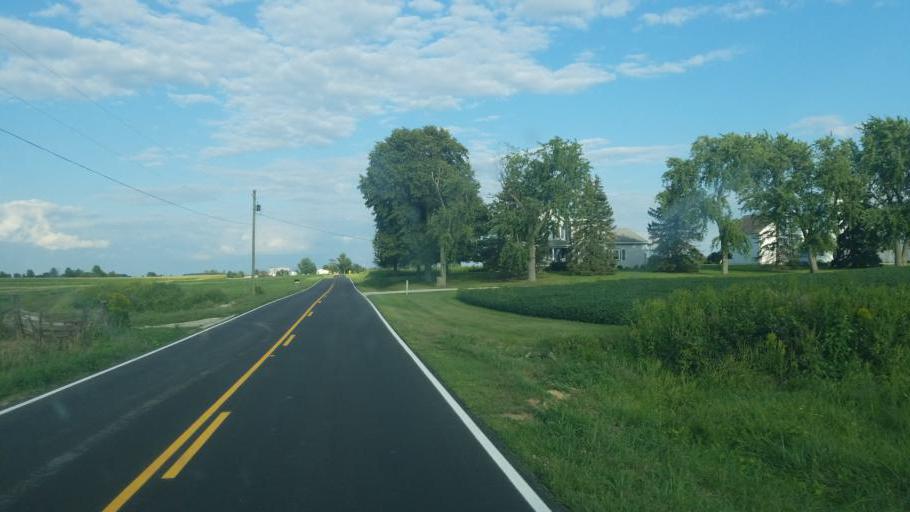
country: US
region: Ohio
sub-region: Seneca County
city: Tiffin
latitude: 41.1100
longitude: -83.0815
